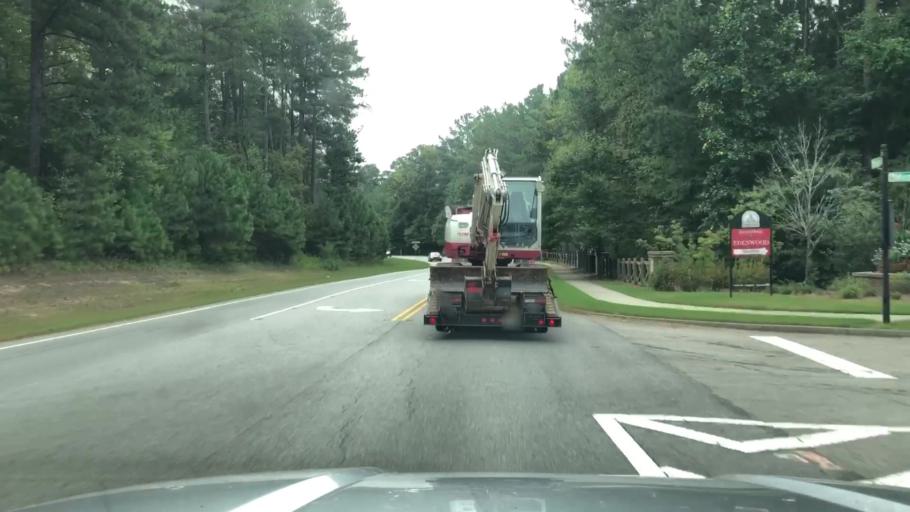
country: US
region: Georgia
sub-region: Bartow County
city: Emerson
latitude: 34.0542
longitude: -84.7969
